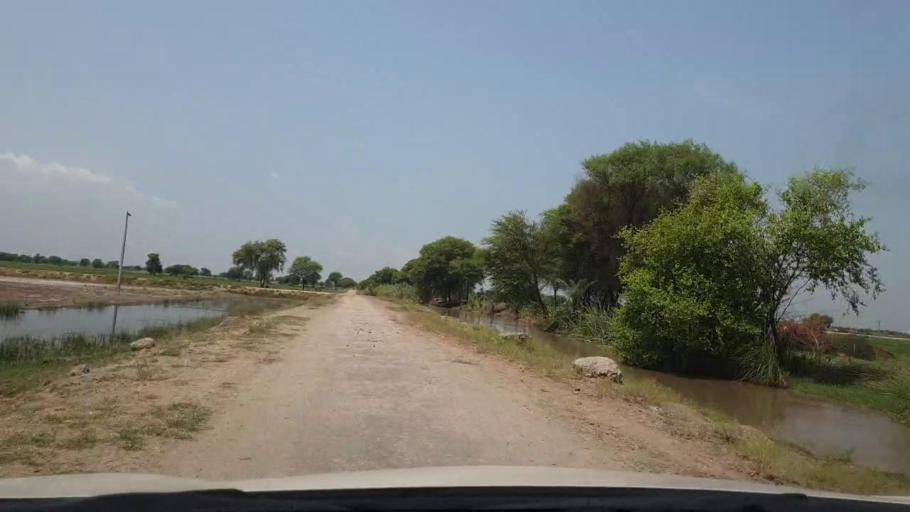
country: PK
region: Sindh
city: Ratodero
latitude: 27.8115
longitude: 68.2445
